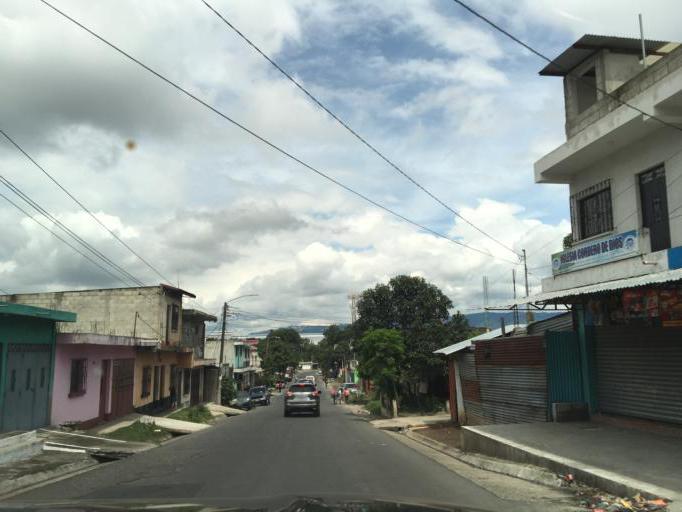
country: GT
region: Guatemala
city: Villa Nueva
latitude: 14.5061
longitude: -90.5876
